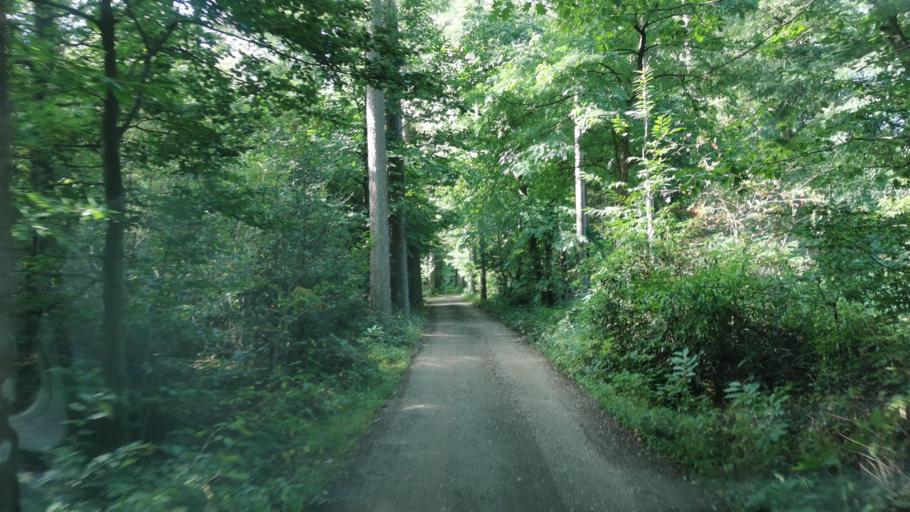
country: NL
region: Overijssel
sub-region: Gemeente Losser
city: Losser
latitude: 52.2766
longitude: 6.9623
